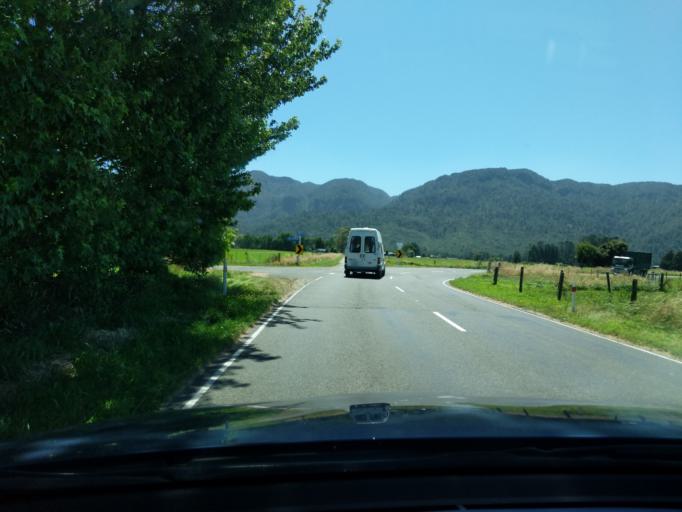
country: NZ
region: Tasman
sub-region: Tasman District
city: Takaka
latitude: -40.7016
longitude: 172.6324
